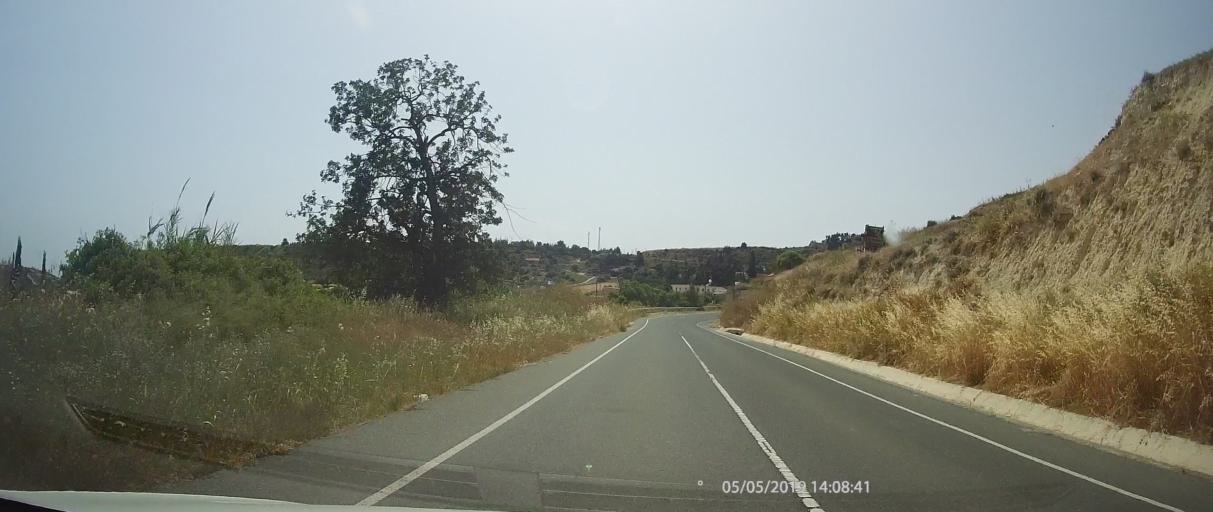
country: CY
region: Limassol
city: Pissouri
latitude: 34.7297
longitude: 32.5802
